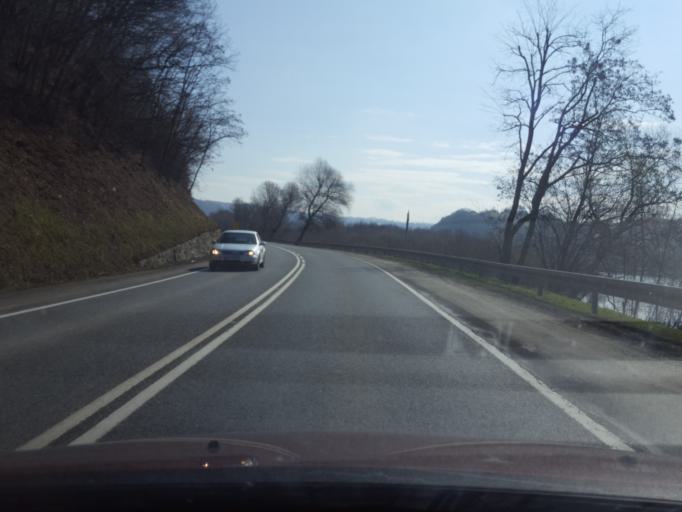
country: PL
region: Lesser Poland Voivodeship
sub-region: Powiat nowosadecki
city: Chelmiec
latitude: 49.6765
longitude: 20.6562
